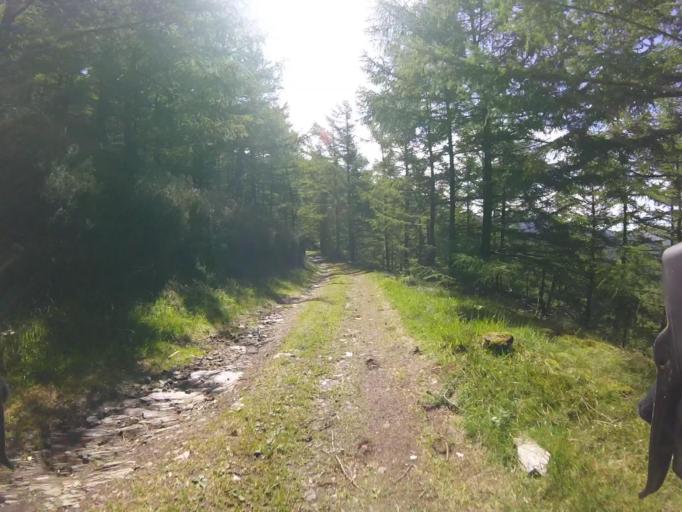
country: ES
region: Navarre
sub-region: Provincia de Navarra
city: Arano
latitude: 43.1840
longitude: -1.9529
